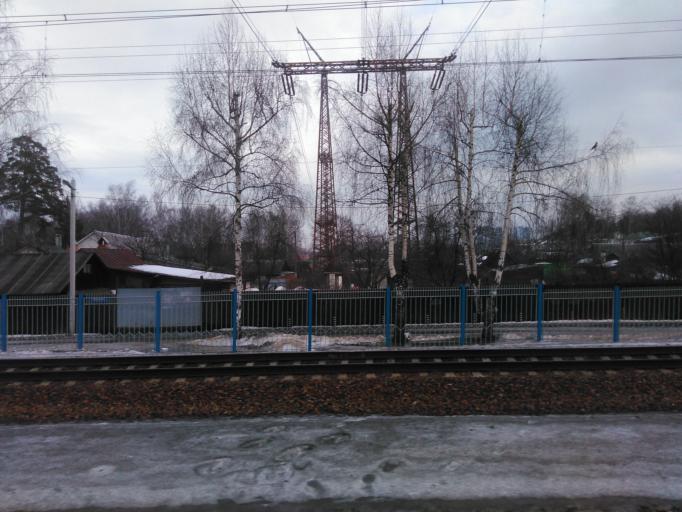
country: RU
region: Moskovskaya
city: Mamontovka
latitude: 55.9588
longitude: 37.8067
